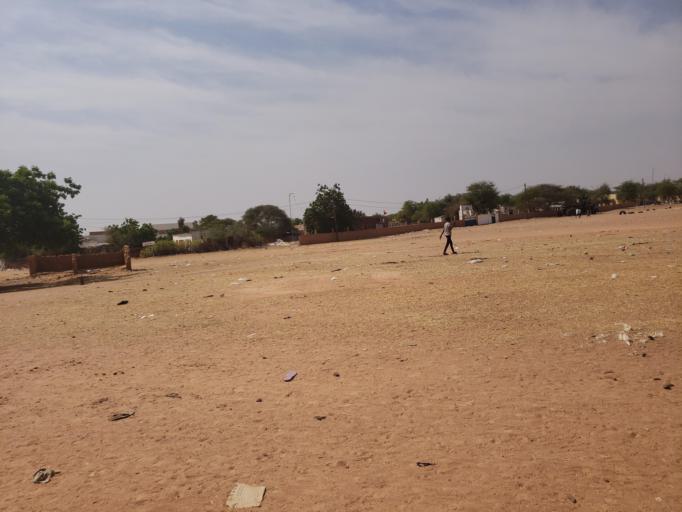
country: SN
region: Matam
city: Ranerou
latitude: 15.2959
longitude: -13.9622
